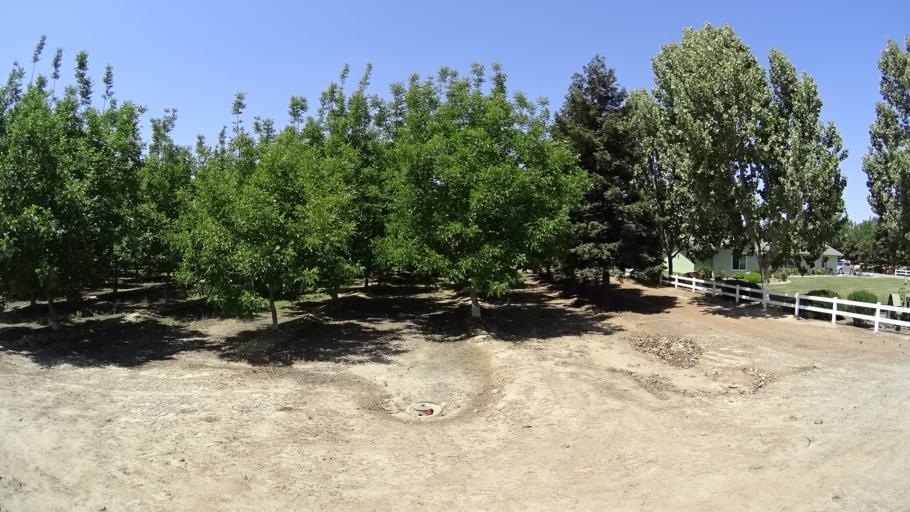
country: US
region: California
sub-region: Kings County
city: Armona
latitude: 36.3013
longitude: -119.7273
